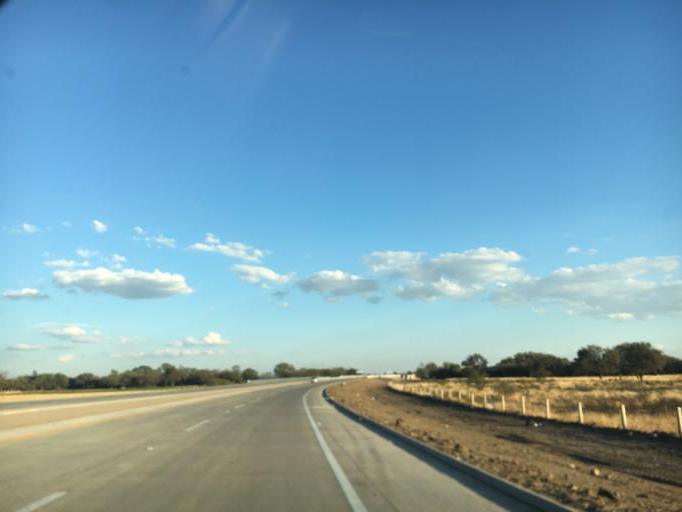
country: MX
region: Guanajuato
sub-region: Leon
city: Ladrilleras del Refugio
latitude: 21.0954
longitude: -101.5658
